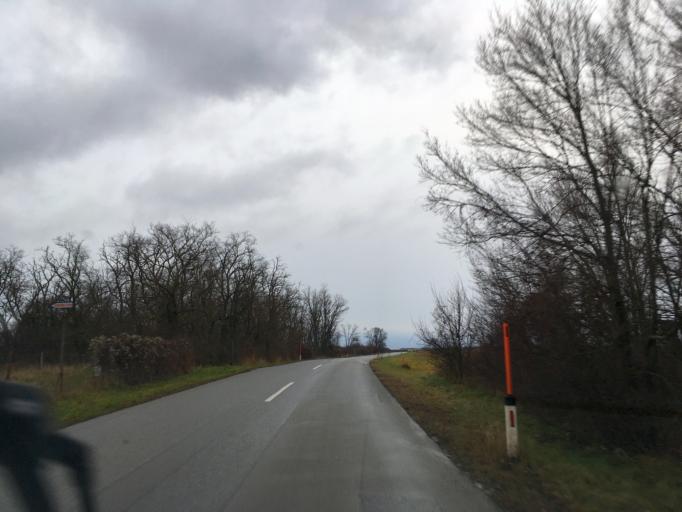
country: AT
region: Lower Austria
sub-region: Politischer Bezirk Wien-Umgebung
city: Rauchenwarth
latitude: 48.0758
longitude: 16.5341
